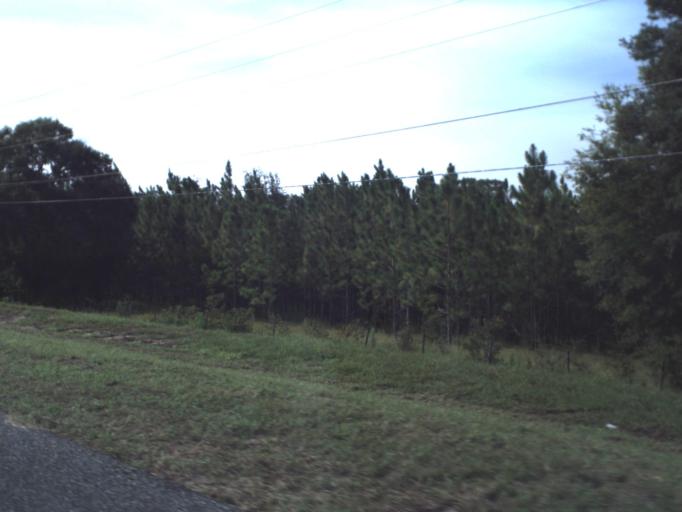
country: US
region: Florida
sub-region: Hernando County
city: Ridge Manor
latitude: 28.5219
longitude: -82.2156
